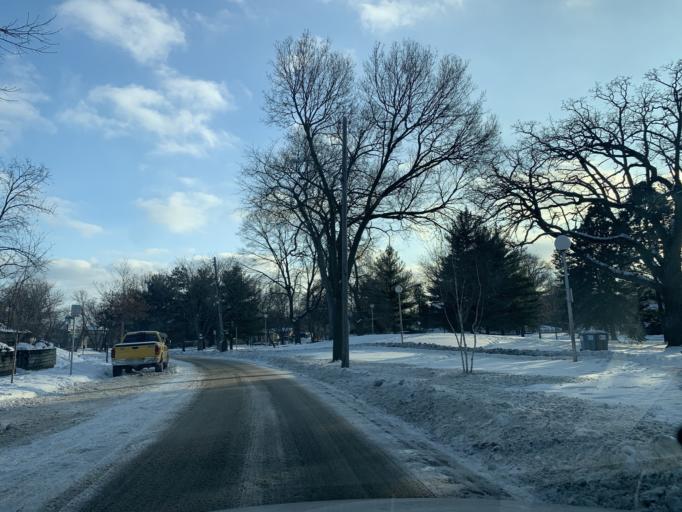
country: US
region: Minnesota
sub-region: Hennepin County
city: Minneapolis
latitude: 44.9886
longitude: -93.3003
